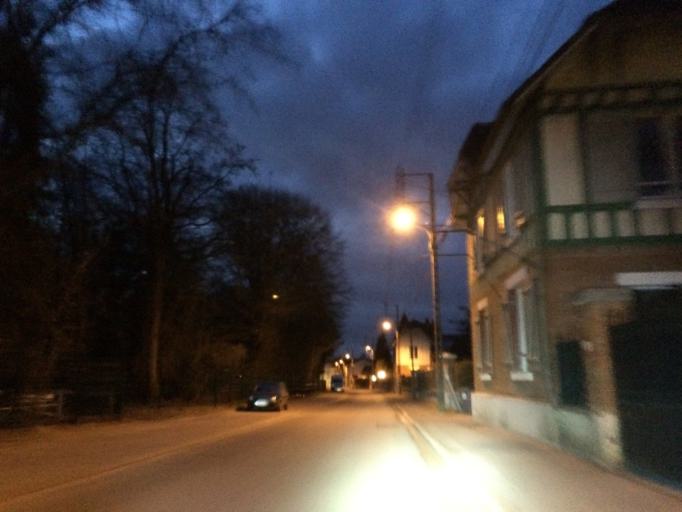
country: FR
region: Picardie
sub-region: Departement de l'Oise
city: Lamorlaye
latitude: 49.1545
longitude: 2.4486
